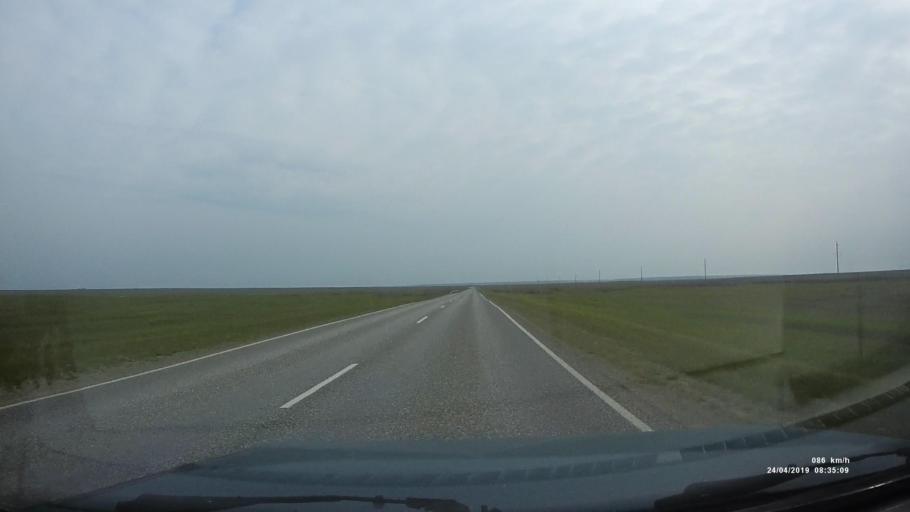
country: RU
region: Kalmykiya
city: Arshan'
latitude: 46.1955
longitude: 43.9149
